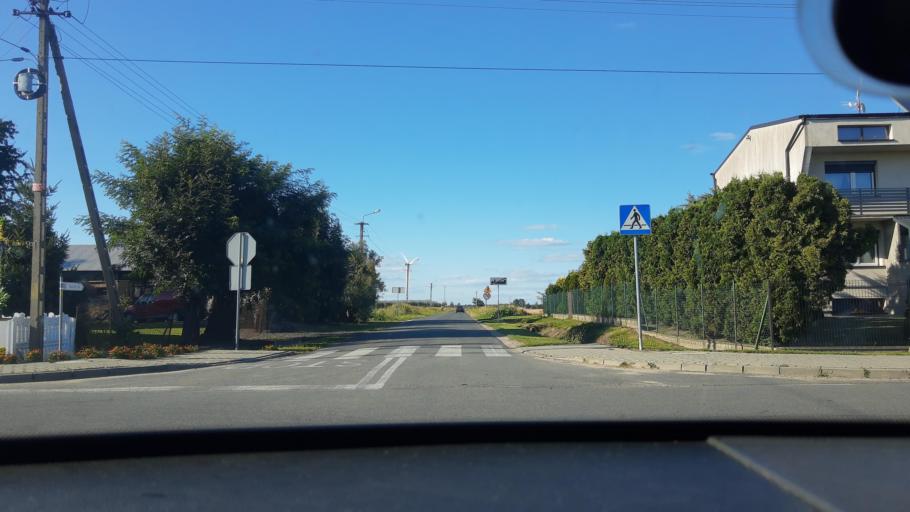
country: PL
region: Lodz Voivodeship
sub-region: Powiat wielunski
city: Wielun
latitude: 51.2550
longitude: 18.6005
